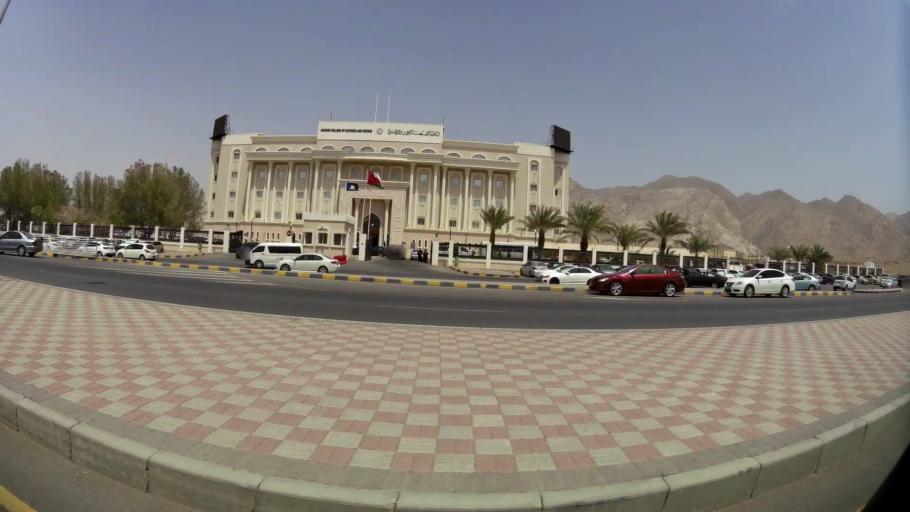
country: OM
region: Muhafazat Masqat
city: Bawshar
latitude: 23.5537
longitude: 58.4004
